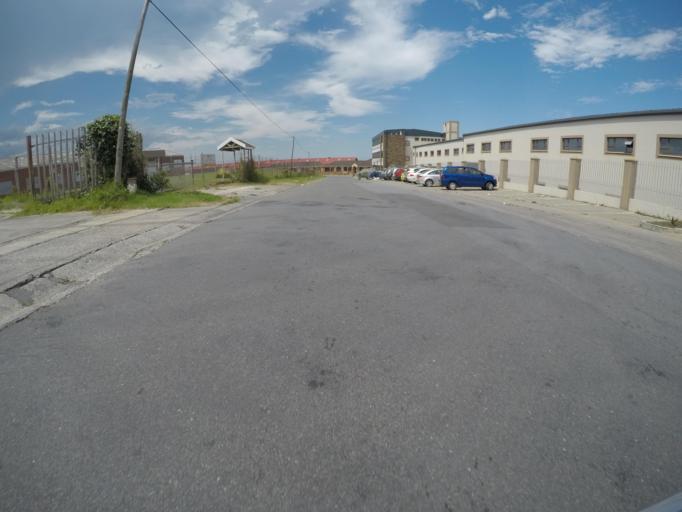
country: ZA
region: Eastern Cape
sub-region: Buffalo City Metropolitan Municipality
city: East London
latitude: -33.0323
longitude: 27.8785
